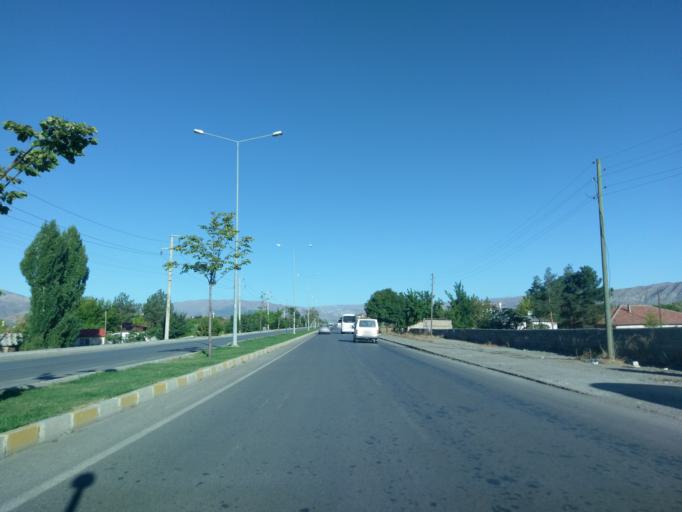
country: TR
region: Erzincan
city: Erzincan
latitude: 39.7529
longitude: 39.4546
